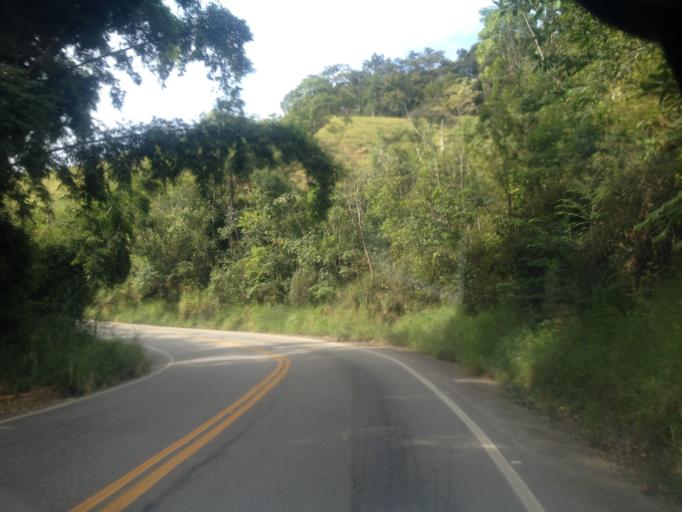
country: BR
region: Rio de Janeiro
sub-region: Quatis
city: Quatis
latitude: -22.3495
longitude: -44.2459
